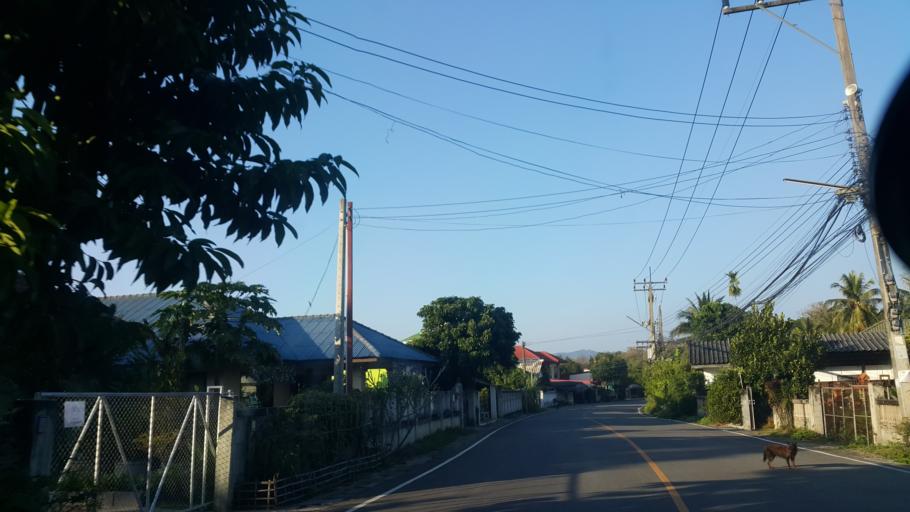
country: TH
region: Chiang Mai
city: San Sai
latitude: 18.8801
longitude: 99.1409
